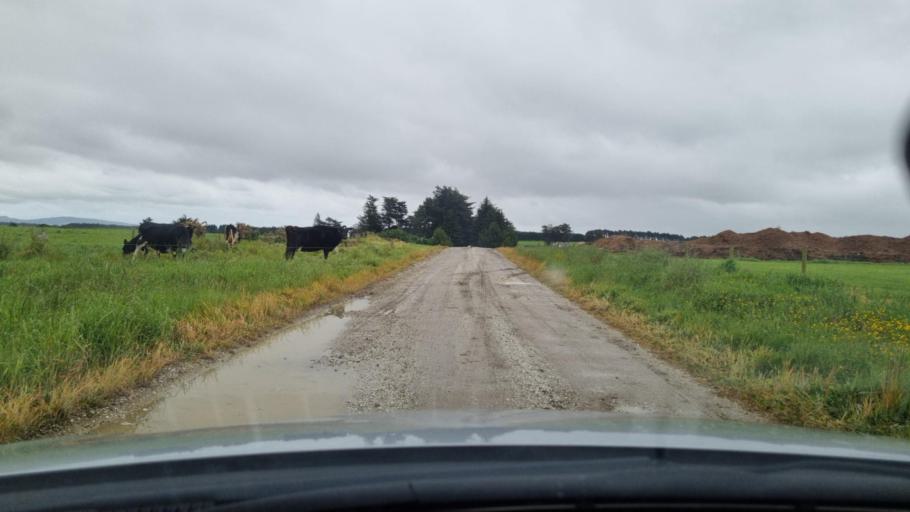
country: NZ
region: Southland
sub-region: Invercargill City
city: Invercargill
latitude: -46.4589
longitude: 168.4202
